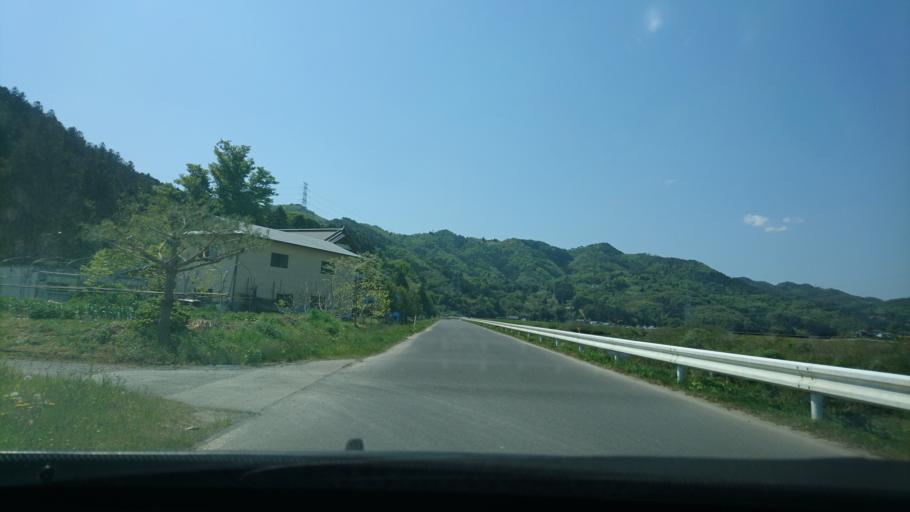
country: JP
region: Iwate
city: Ichinoseki
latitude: 38.9290
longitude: 141.2531
